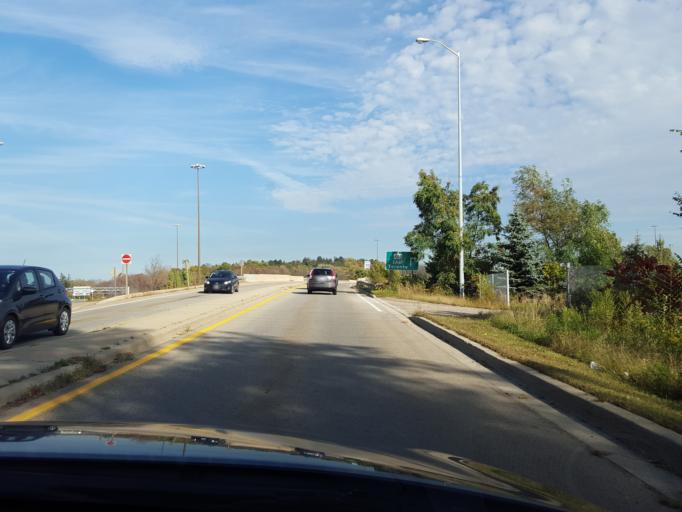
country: CA
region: Ontario
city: Ancaster
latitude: 43.2322
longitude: -79.9548
